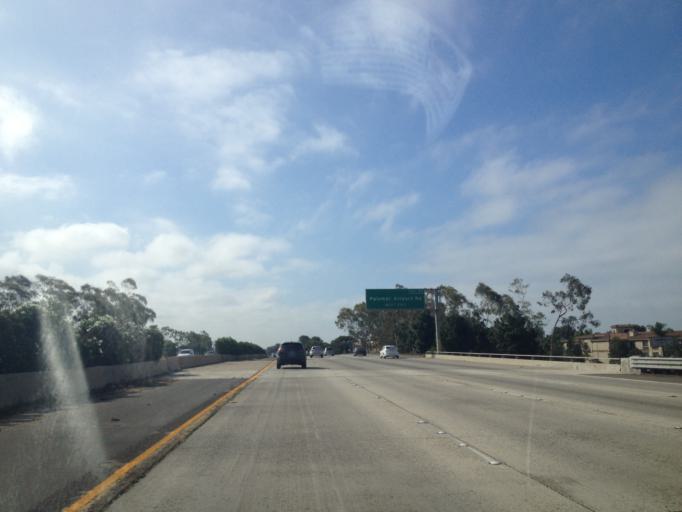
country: US
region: California
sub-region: San Diego County
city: Carlsbad
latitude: 33.1352
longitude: -117.3298
